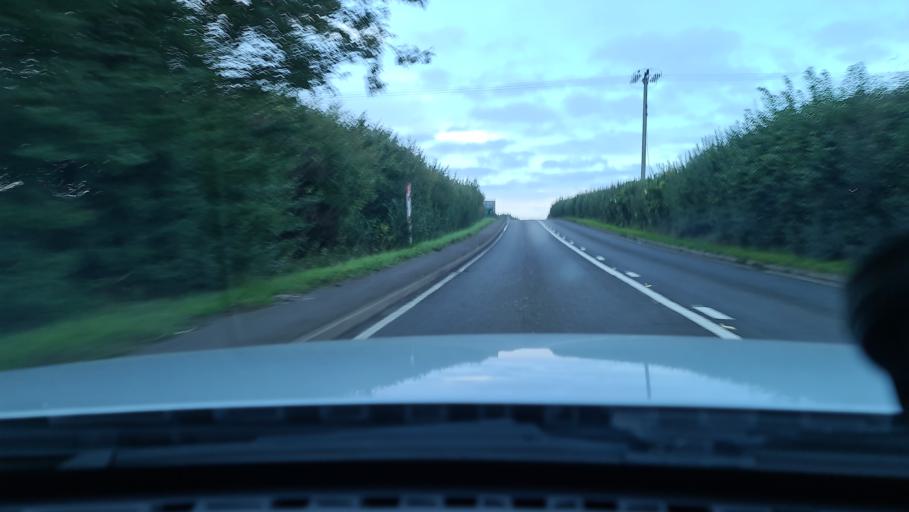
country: GB
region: England
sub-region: Warwickshire
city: Ryton on Dunsmore
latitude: 52.3313
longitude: -1.4111
